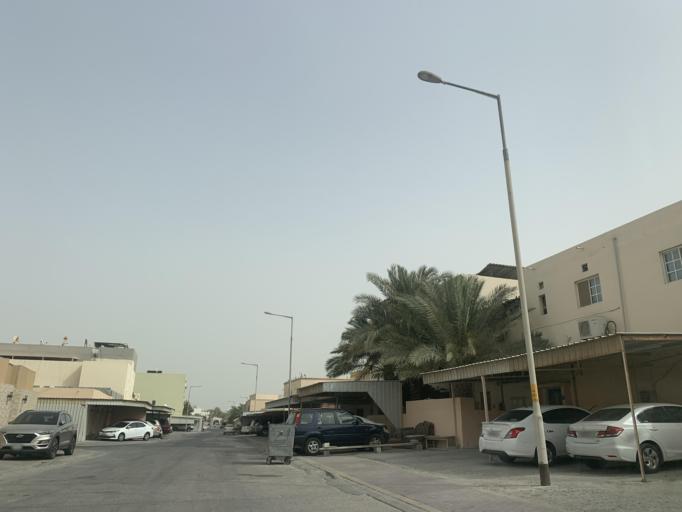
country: BH
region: Northern
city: Madinat `Isa
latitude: 26.1652
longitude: 50.5672
